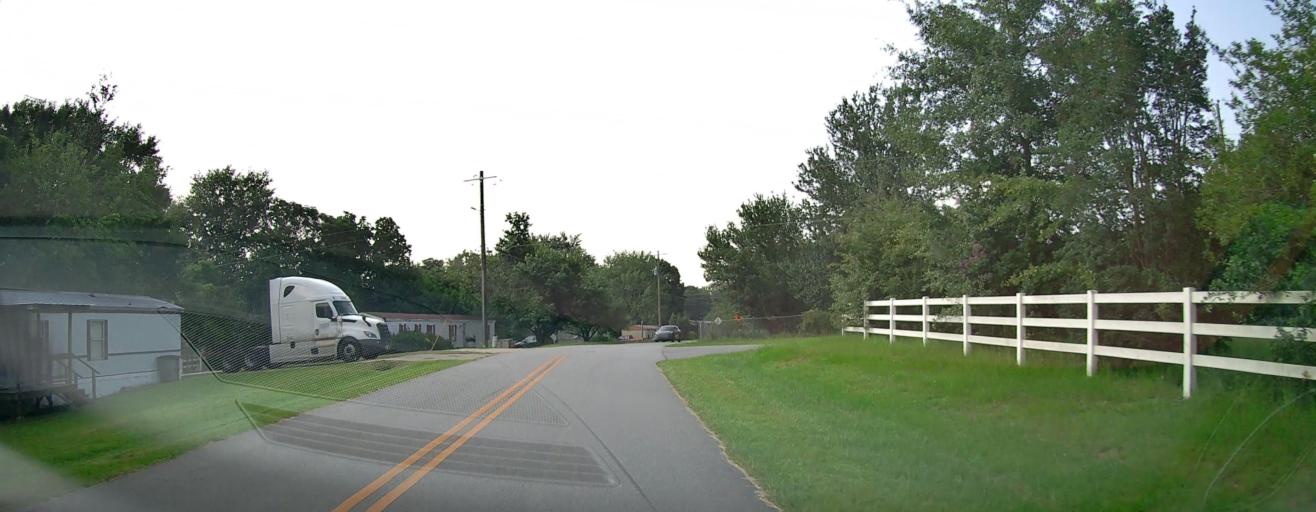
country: US
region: Georgia
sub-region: Houston County
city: Centerville
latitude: 32.6414
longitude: -83.6833
